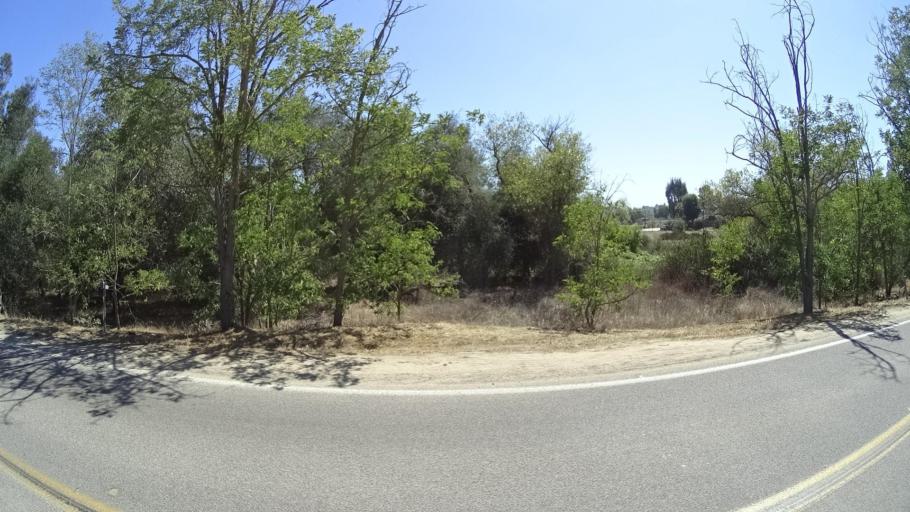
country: US
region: California
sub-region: San Diego County
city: Hidden Meadows
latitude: 33.2694
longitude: -117.1081
